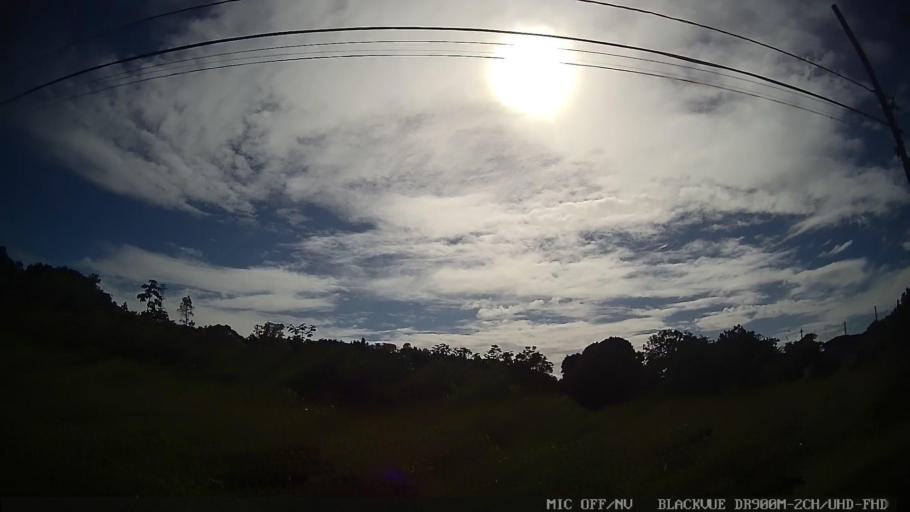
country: BR
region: Sao Paulo
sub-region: Peruibe
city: Peruibe
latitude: -24.2422
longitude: -46.9122
